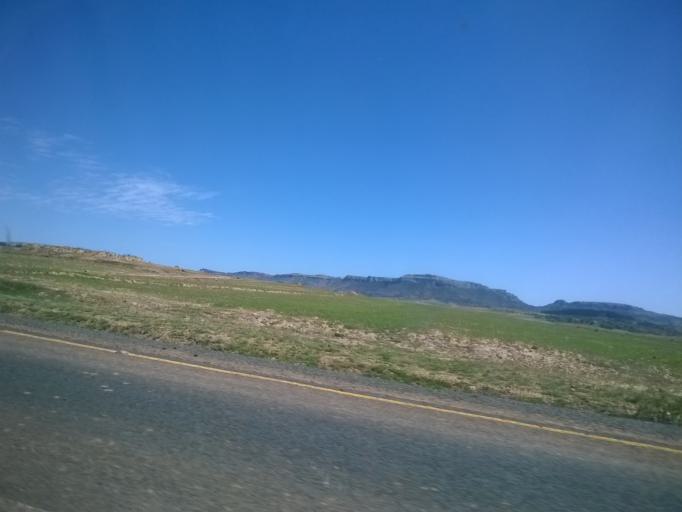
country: LS
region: Berea
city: Teyateyaneng
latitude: -29.0826
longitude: 27.9043
